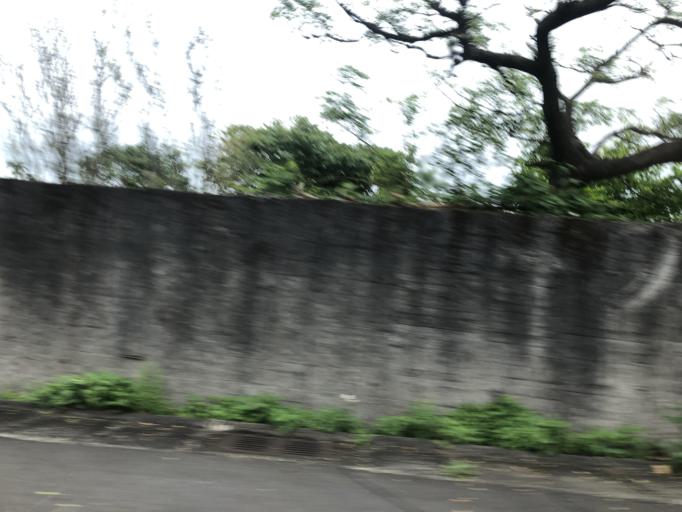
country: TW
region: Taiwan
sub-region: Keelung
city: Keelung
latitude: 25.2159
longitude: 121.6479
